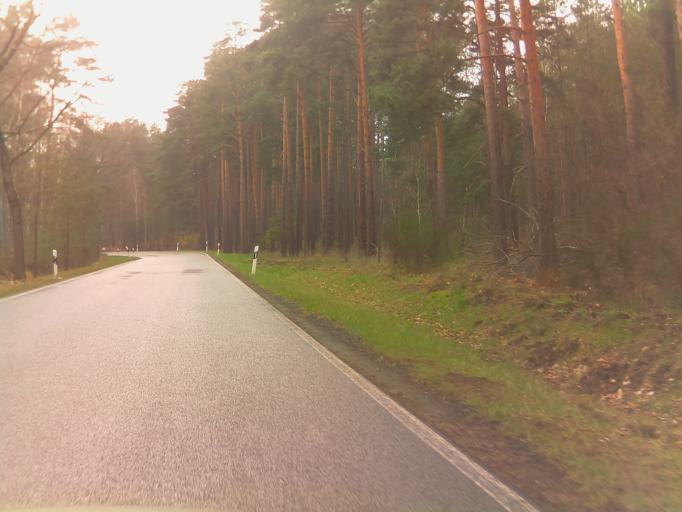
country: DE
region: Brandenburg
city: Schlepzig
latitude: 52.0327
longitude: 13.8053
